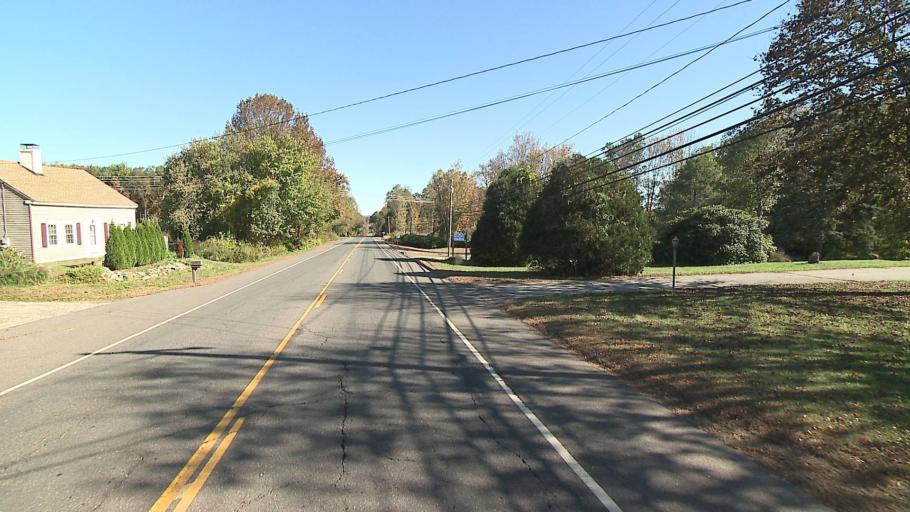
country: US
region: Connecticut
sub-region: Tolland County
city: Hebron
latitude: 41.6957
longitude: -72.3102
